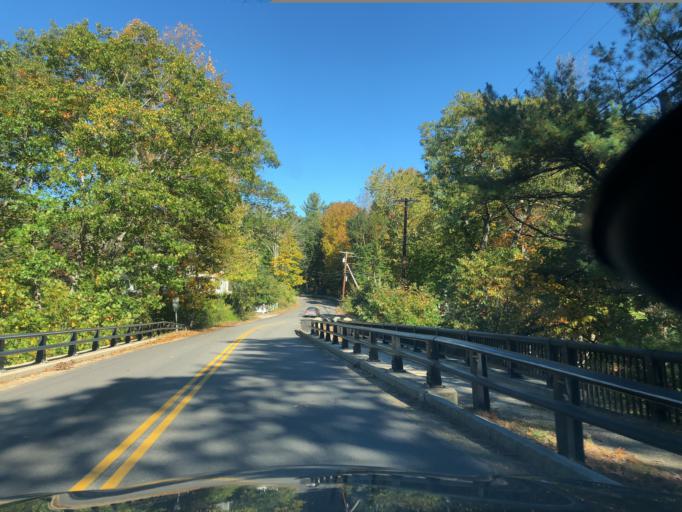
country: US
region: New Hampshire
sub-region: Rockingham County
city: Newmarket
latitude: 43.1027
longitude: -70.9518
